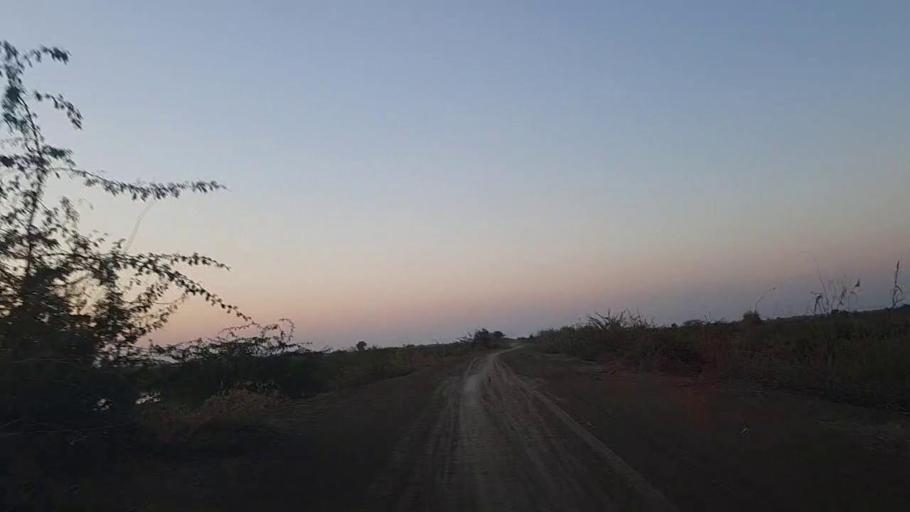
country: PK
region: Sindh
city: Tando Mittha Khan
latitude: 26.0642
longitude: 69.1623
